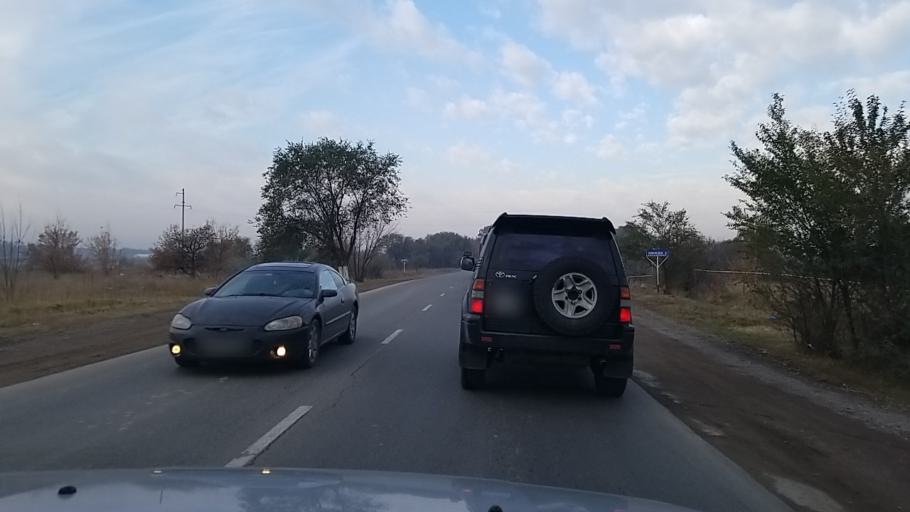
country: KZ
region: Almaty Oblysy
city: Burunday
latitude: 43.3605
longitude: 76.7461
